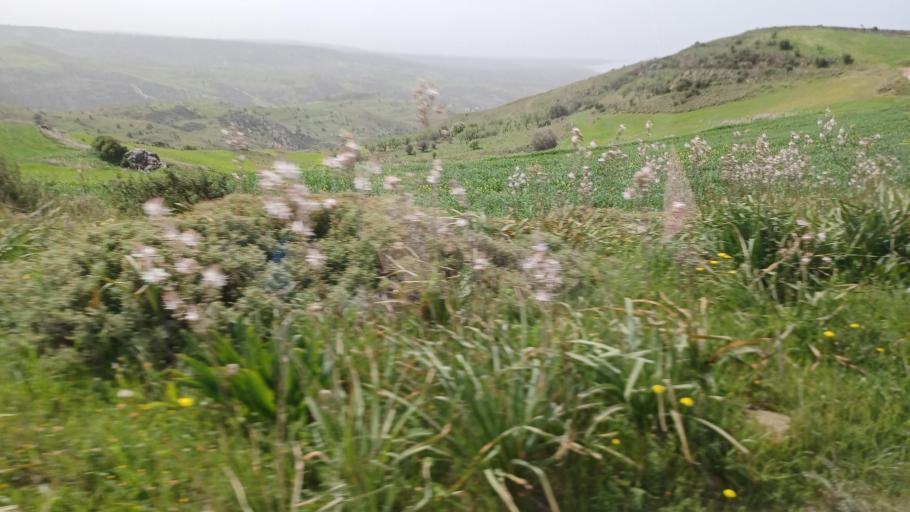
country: CY
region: Pafos
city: Polis
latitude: 34.9759
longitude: 32.3485
